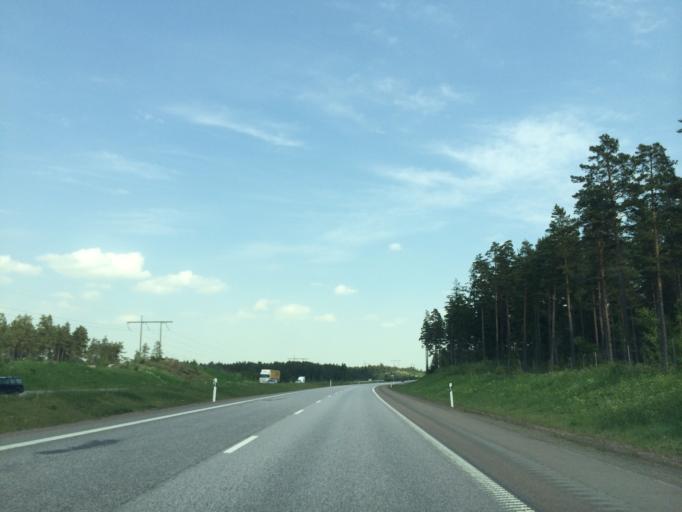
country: SE
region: OEstergoetland
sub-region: Vadstena Kommun
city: Herrestad
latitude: 58.2598
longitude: 14.8342
